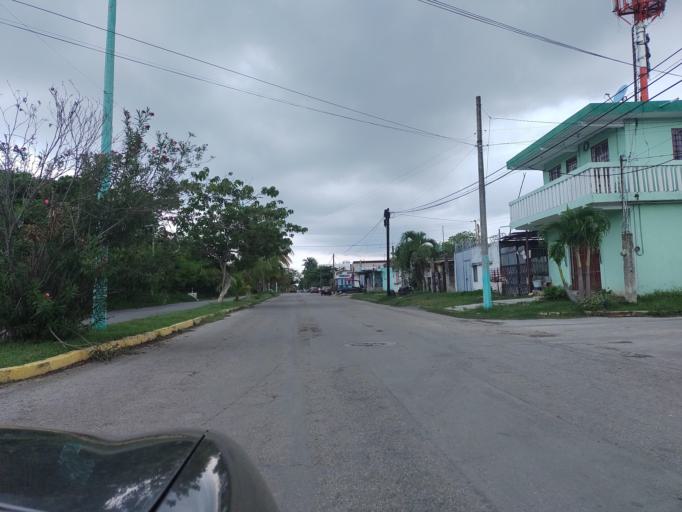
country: MX
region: Quintana Roo
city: Chetumal
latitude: 18.5176
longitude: -88.2773
